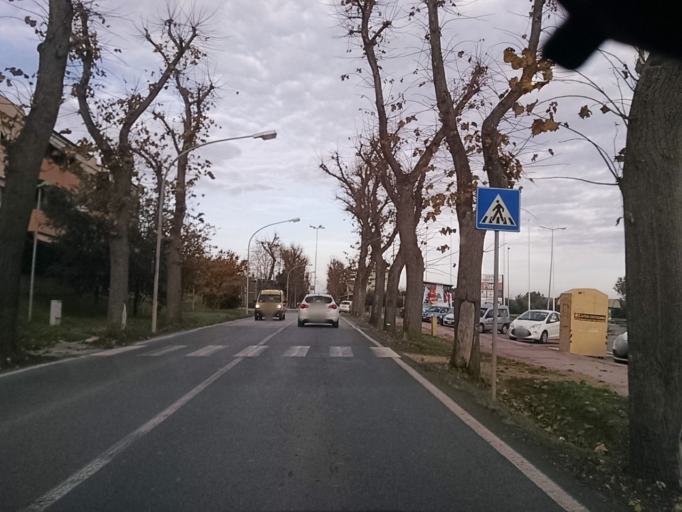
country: IT
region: Tuscany
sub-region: Provincia di Grosseto
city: Follonica
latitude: 42.9333
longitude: 10.7741
